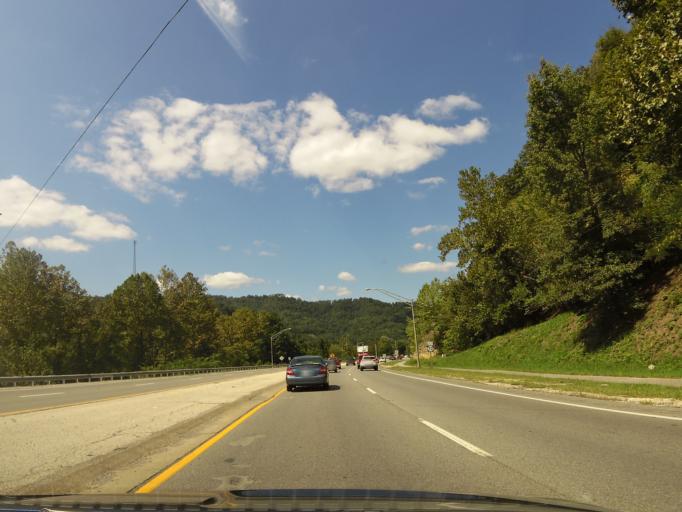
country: US
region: Kentucky
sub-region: Harlan County
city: Harlan
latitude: 36.8273
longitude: -83.3232
